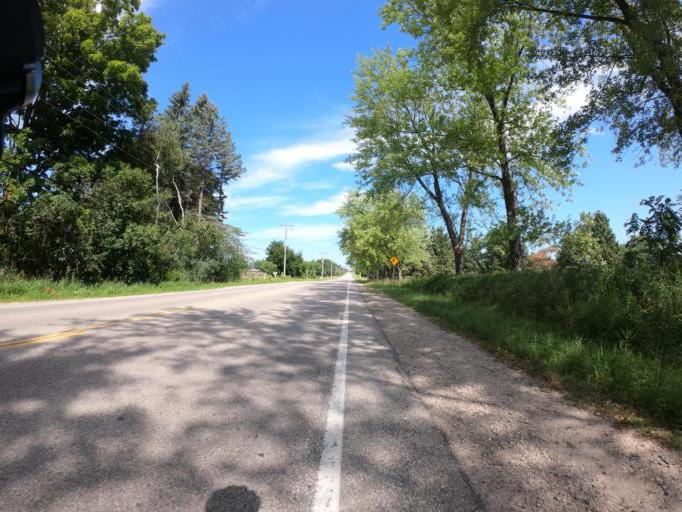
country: CA
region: Ontario
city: Waterloo
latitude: 43.5133
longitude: -80.3935
